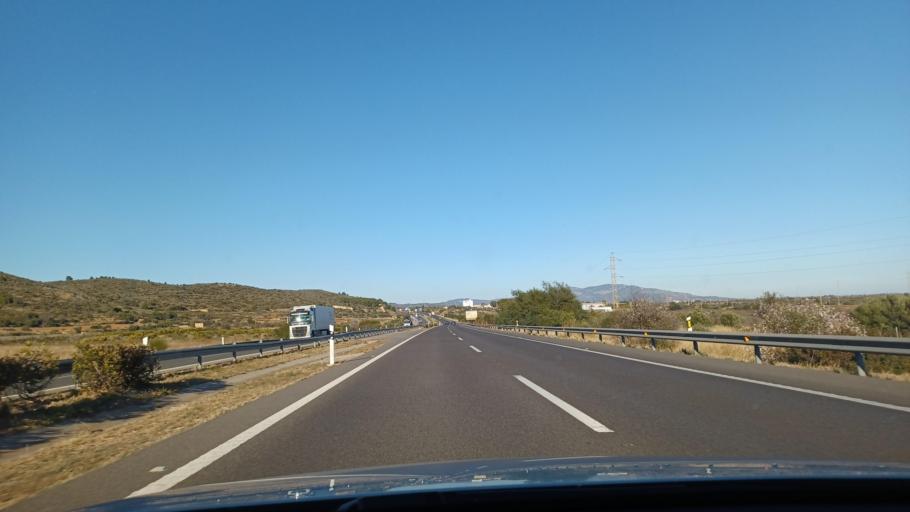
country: ES
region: Valencia
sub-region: Provincia de Castello
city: Torreblanca
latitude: 40.1823
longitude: 0.1669
